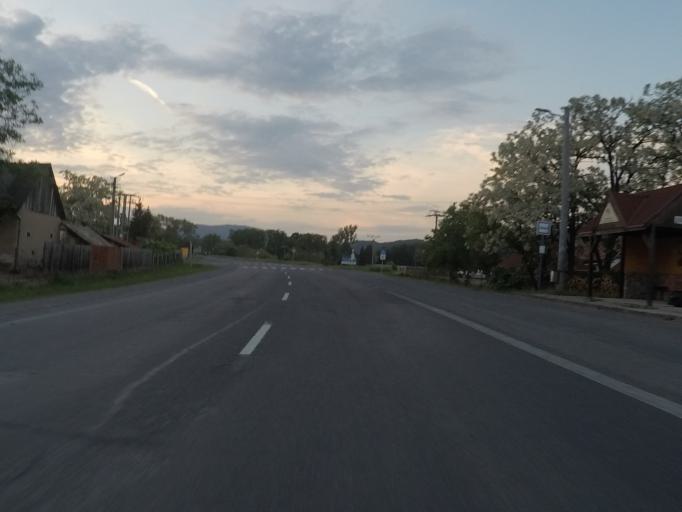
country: SK
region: Banskobystricky
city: Rimavska Sobota
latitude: 48.4635
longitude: 19.9537
